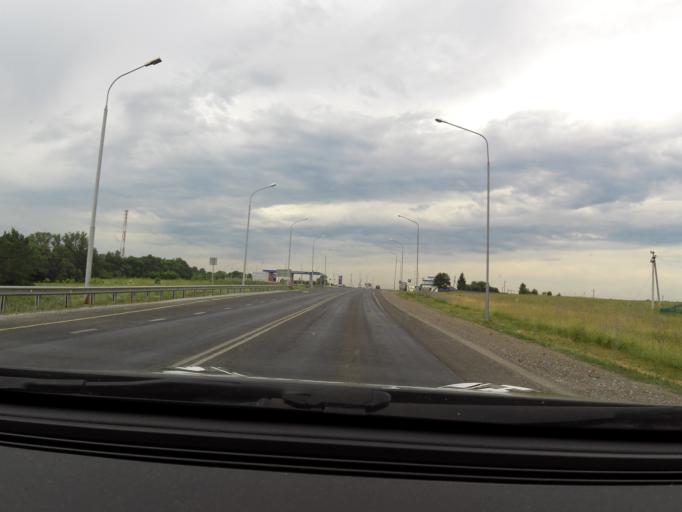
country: RU
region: Bashkortostan
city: Urman
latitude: 54.8208
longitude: 56.8815
